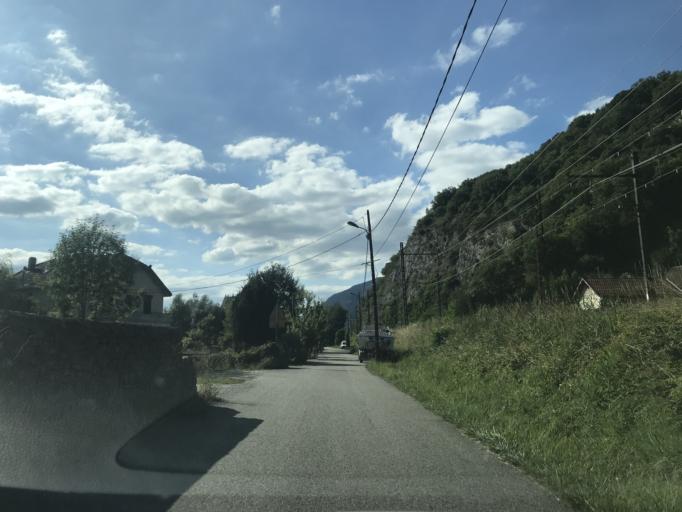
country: FR
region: Rhone-Alpes
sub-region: Departement de l'Ain
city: Culoz
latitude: 45.8251
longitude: 5.8058
